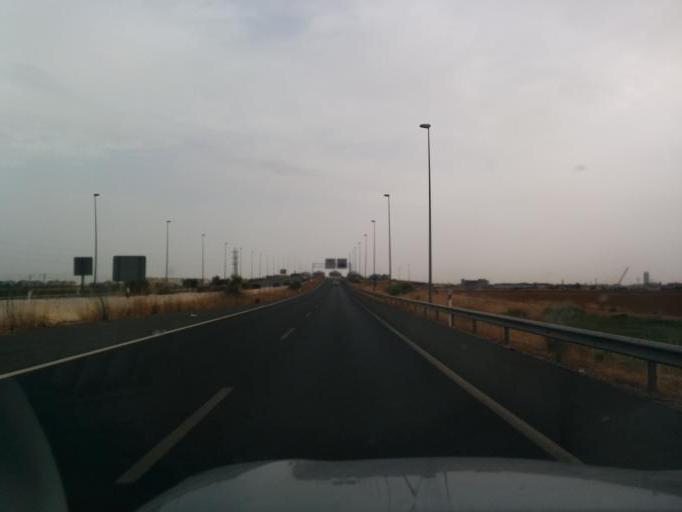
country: ES
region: Andalusia
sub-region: Provincia de Sevilla
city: La Rinconada
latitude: 37.4432
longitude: -5.9717
